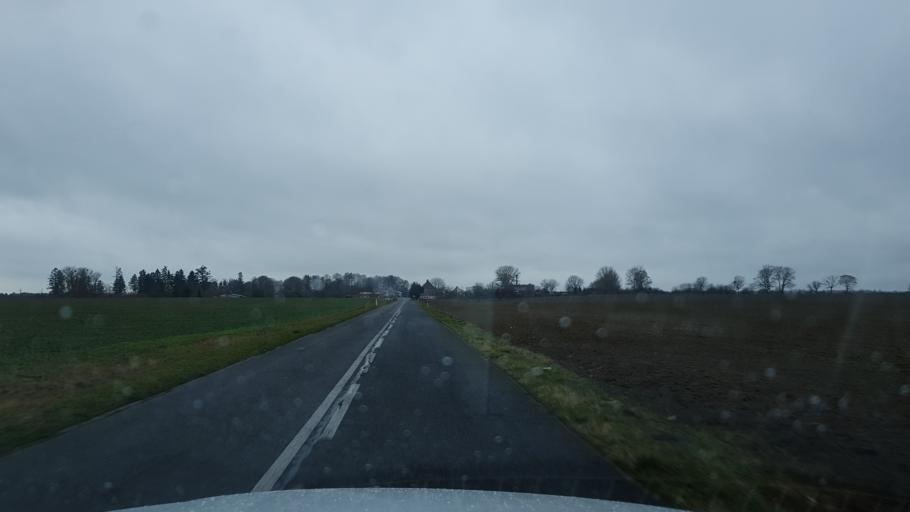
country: PL
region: West Pomeranian Voivodeship
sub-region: Powiat lobeski
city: Radowo Male
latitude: 53.6277
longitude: 15.5027
